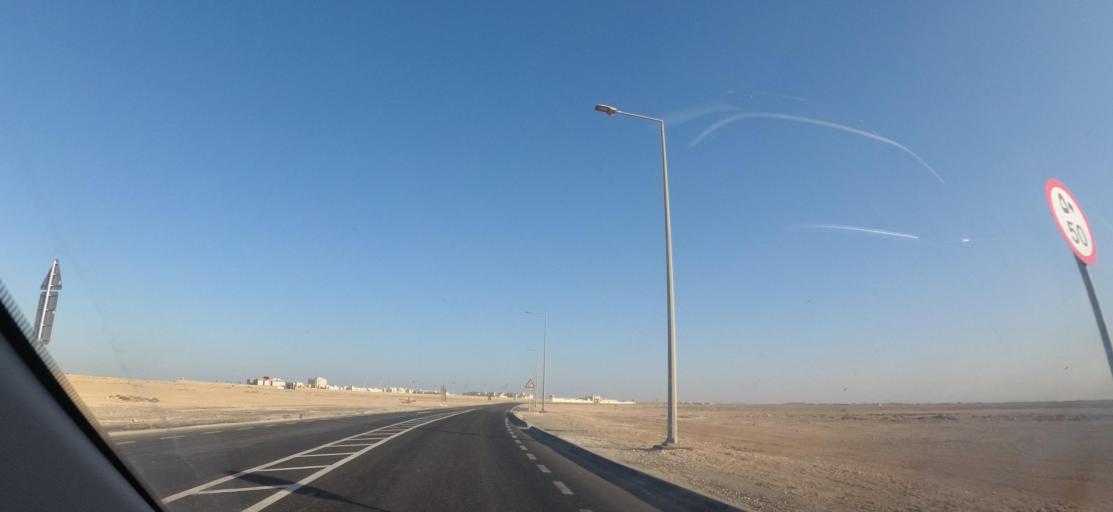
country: QA
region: Madinat ash Shamal
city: Ar Ru'ays
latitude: 26.1333
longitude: 51.2290
